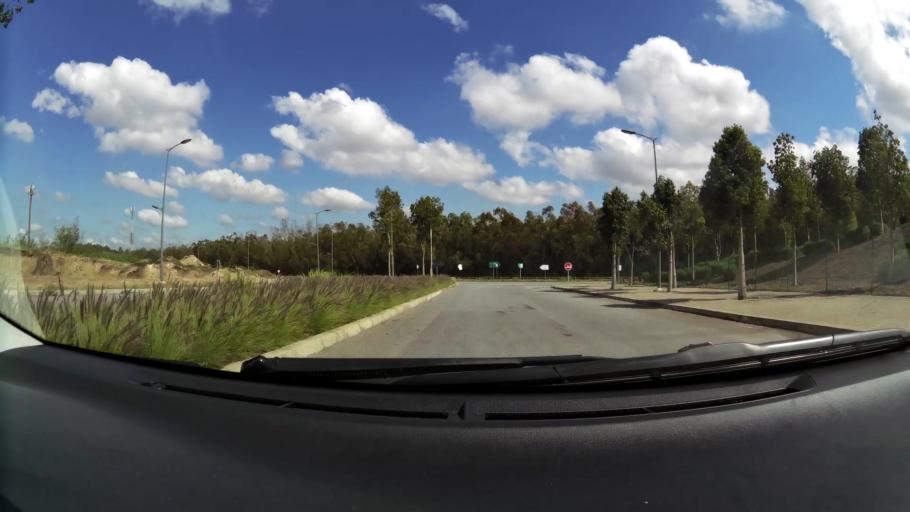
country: MA
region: Grand Casablanca
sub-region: Nouaceur
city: Bouskoura
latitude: 33.4810
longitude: -7.5872
